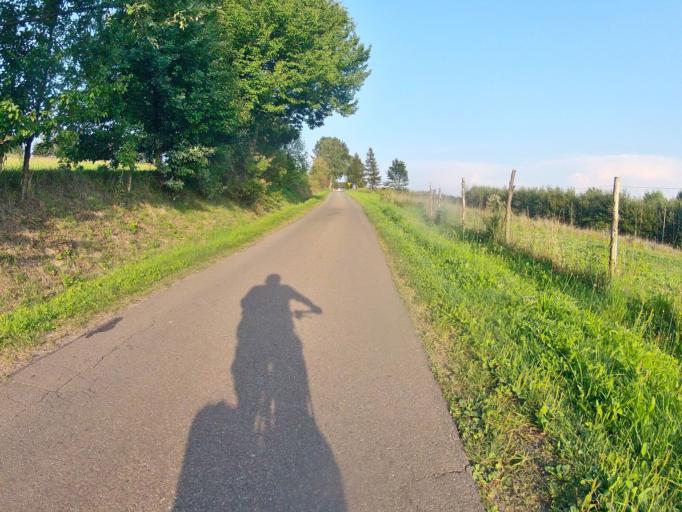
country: PL
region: Subcarpathian Voivodeship
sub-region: Powiat jasielski
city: Brzyska
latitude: 49.7886
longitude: 21.3752
